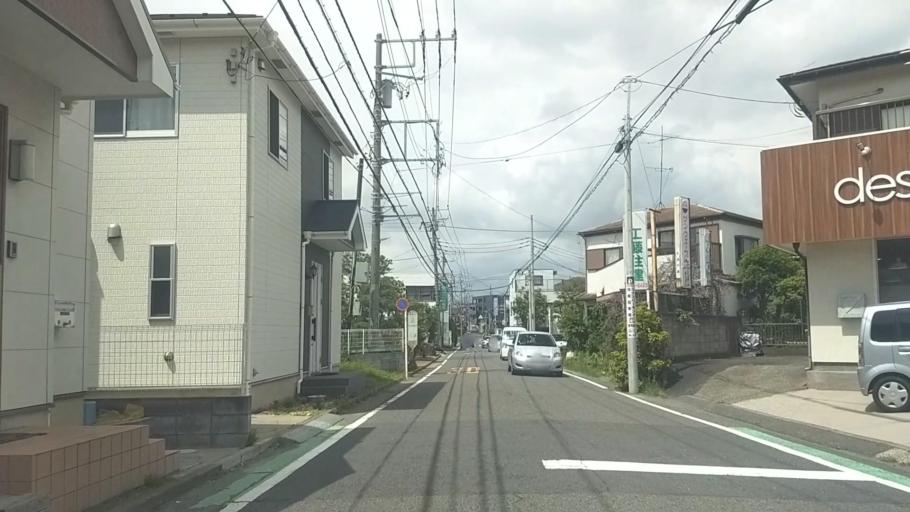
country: JP
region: Kanagawa
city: Fujisawa
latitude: 35.3441
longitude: 139.4552
